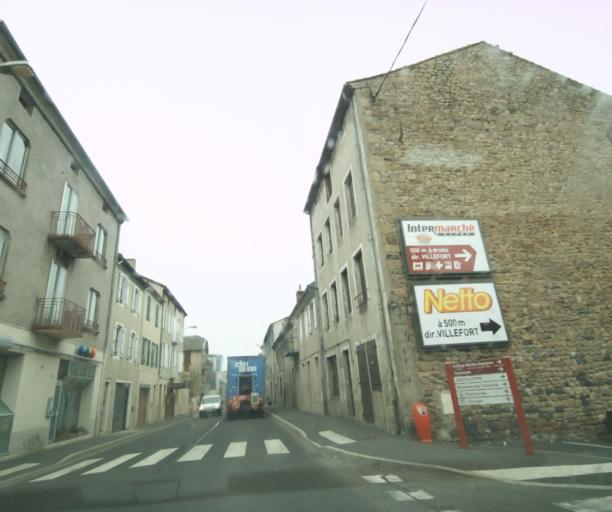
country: FR
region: Languedoc-Roussillon
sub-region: Departement de la Lozere
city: Langogne
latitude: 44.7239
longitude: 3.8521
